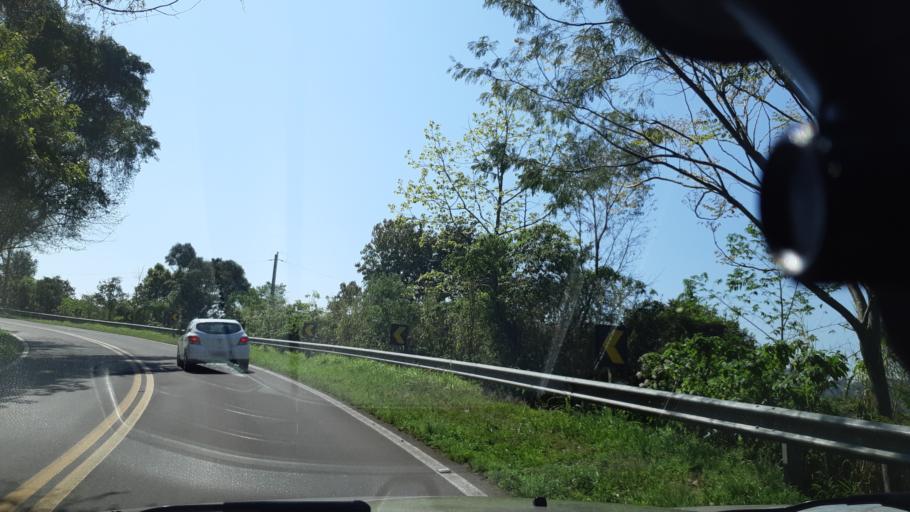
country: BR
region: Rio Grande do Sul
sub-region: Nova Petropolis
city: Nova Petropolis
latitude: -29.4051
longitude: -51.1246
